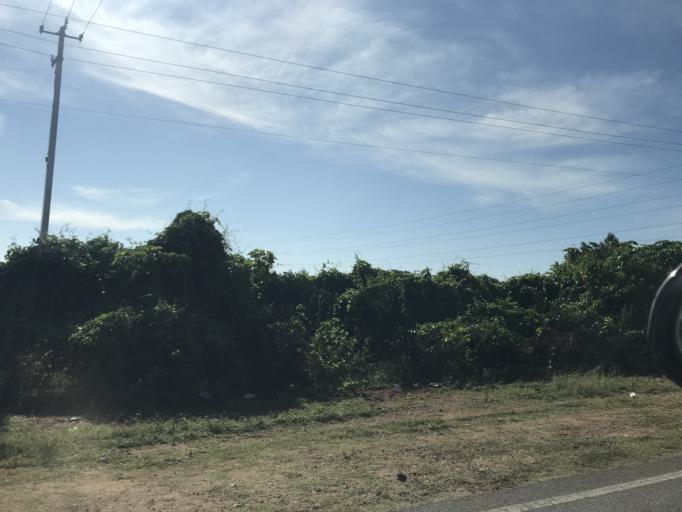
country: IN
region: Karnataka
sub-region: Mysore
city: Mysore
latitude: 12.2204
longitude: 76.5735
